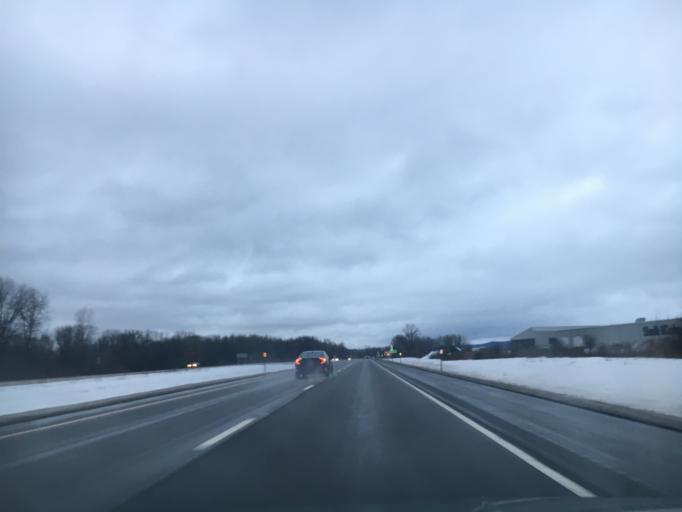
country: US
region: New York
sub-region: Cortland County
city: Homer
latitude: 42.7552
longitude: -76.1351
